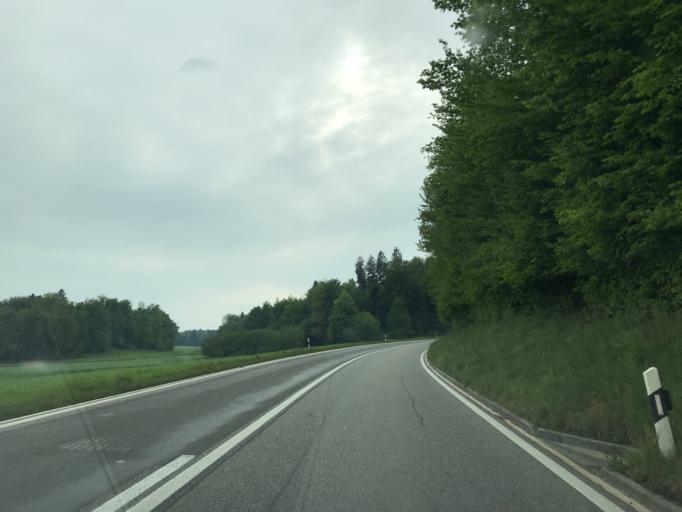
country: CH
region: Bern
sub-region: Oberaargau
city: Aarwangen
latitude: 47.2492
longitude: 7.7417
